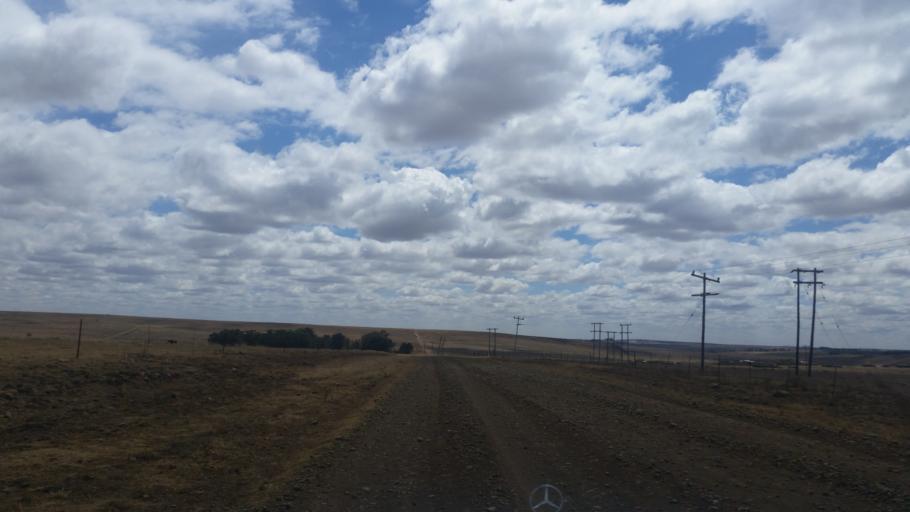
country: ZA
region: Orange Free State
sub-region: Thabo Mofutsanyana District Municipality
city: Harrismith
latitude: -28.2375
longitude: 28.9291
